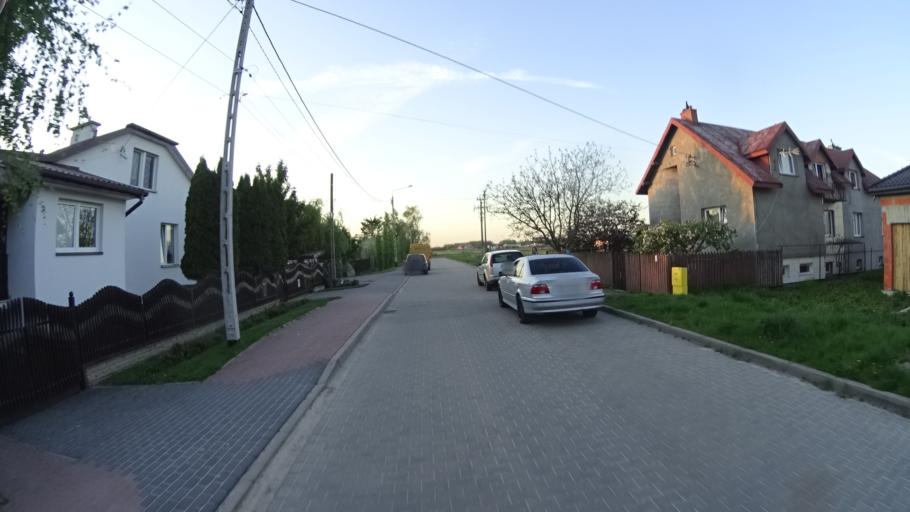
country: PL
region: Masovian Voivodeship
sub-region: Powiat warszawski zachodni
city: Ozarow Mazowiecki
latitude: 52.2218
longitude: 20.7792
